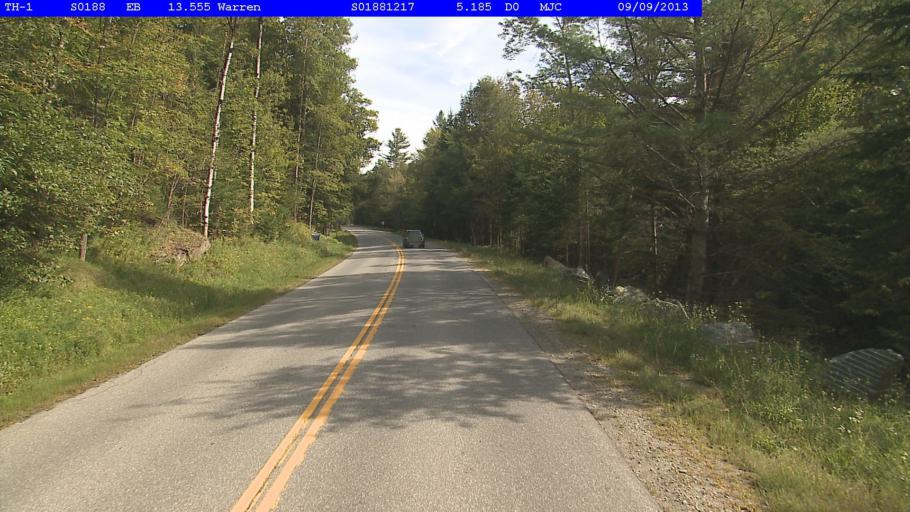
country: US
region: Vermont
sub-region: Washington County
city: Northfield
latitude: 44.1081
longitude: -72.8409
